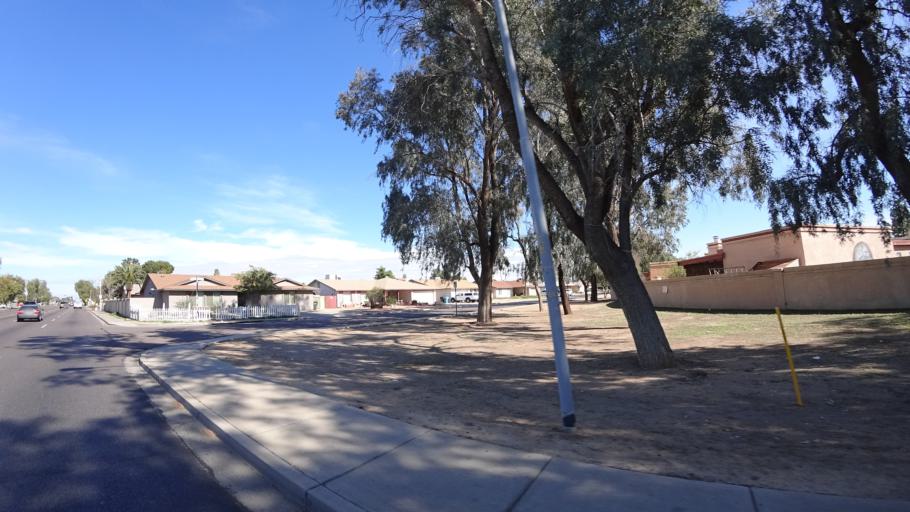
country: US
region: Arizona
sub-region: Maricopa County
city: Glendale
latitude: 33.5047
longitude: -112.2031
